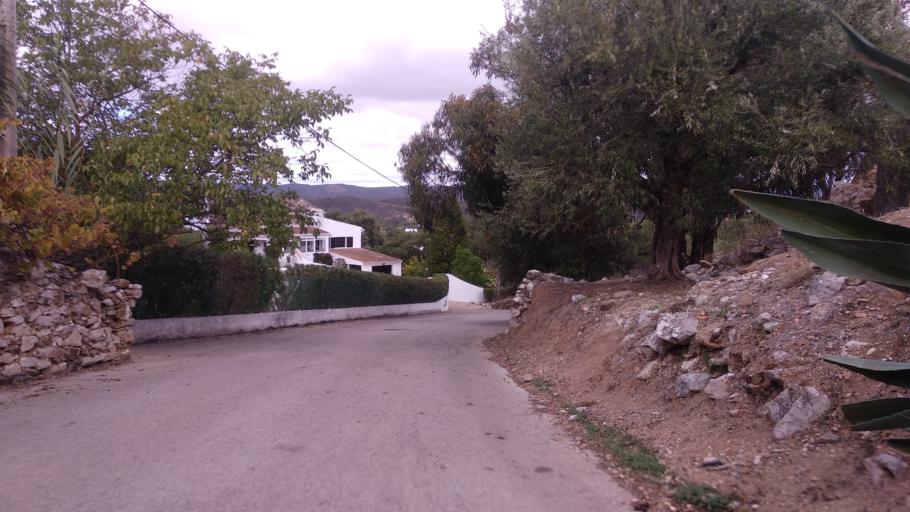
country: PT
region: Faro
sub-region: Sao Bras de Alportel
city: Sao Bras de Alportel
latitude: 37.1637
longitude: -7.9059
